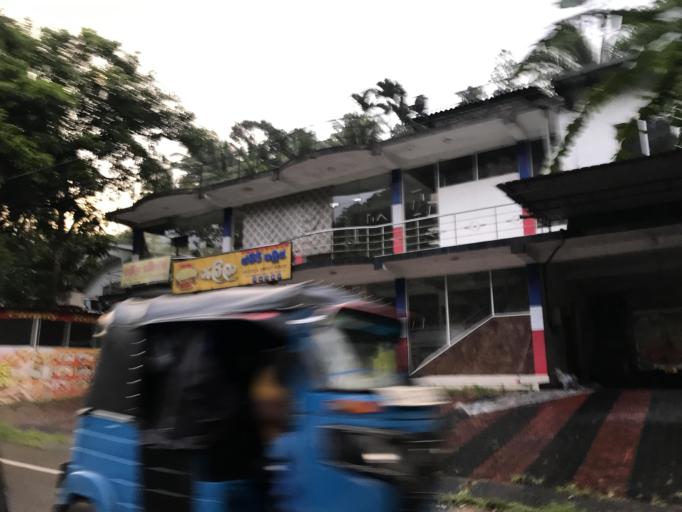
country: LK
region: Western
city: Horawala Junction
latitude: 6.5214
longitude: 80.2036
